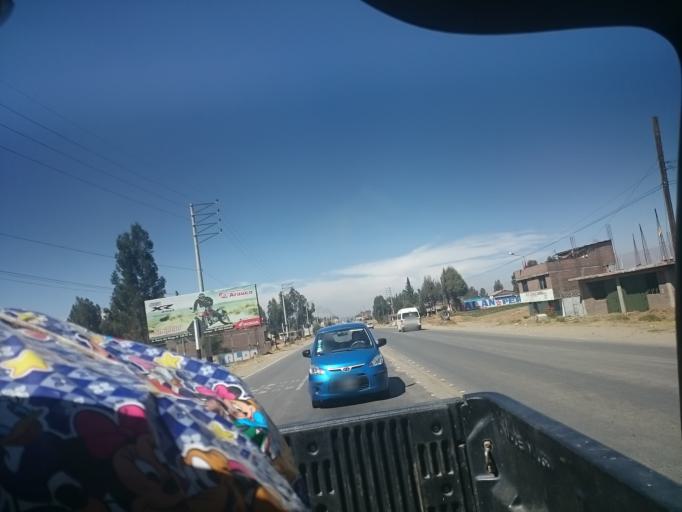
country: PE
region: Junin
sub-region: Provincia de Huancayo
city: San Jeronimo
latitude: -11.9604
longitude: -75.2747
